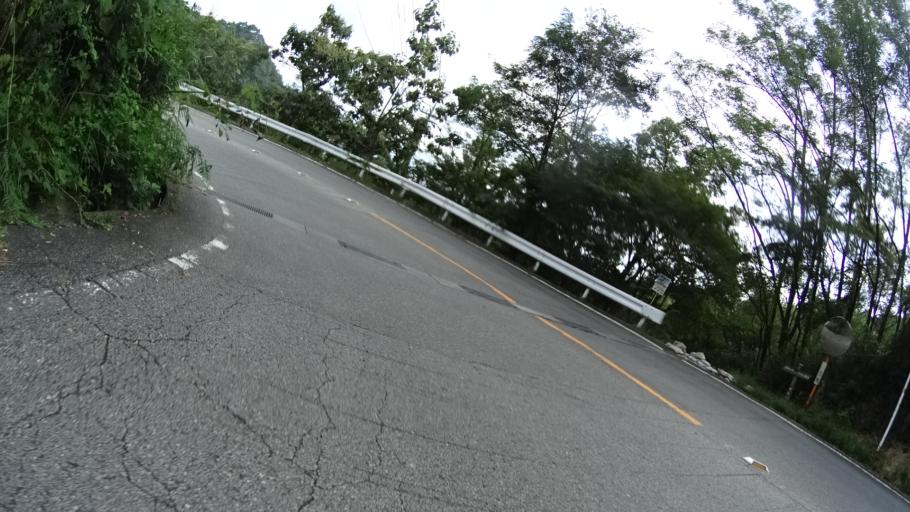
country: JP
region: Yamanashi
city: Kofu-shi
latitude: 35.6969
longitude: 138.5605
